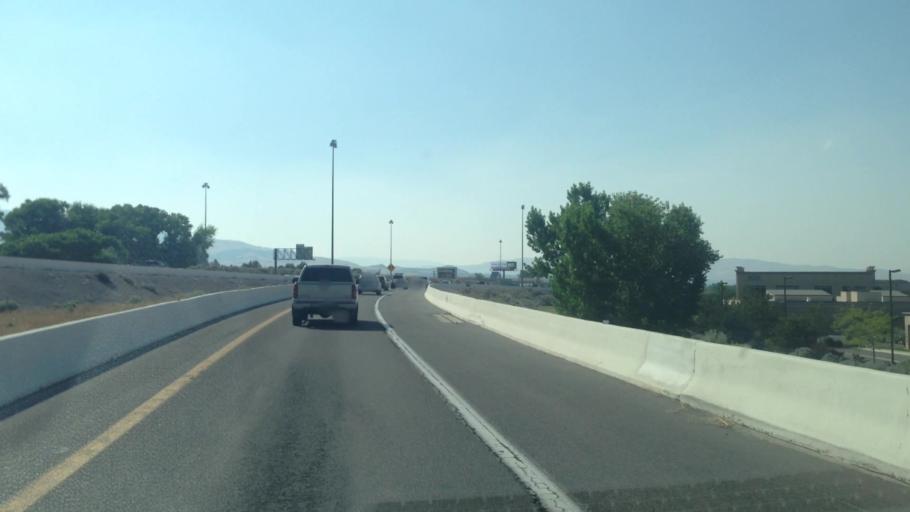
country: US
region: Nevada
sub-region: Washoe County
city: Sparks
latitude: 39.4247
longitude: -119.7532
